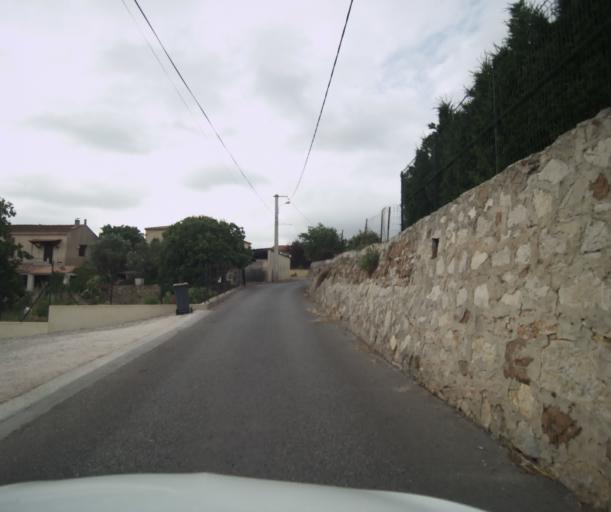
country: FR
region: Provence-Alpes-Cote d'Azur
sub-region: Departement du Var
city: La Seyne-sur-Mer
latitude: 43.1194
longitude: 5.8805
